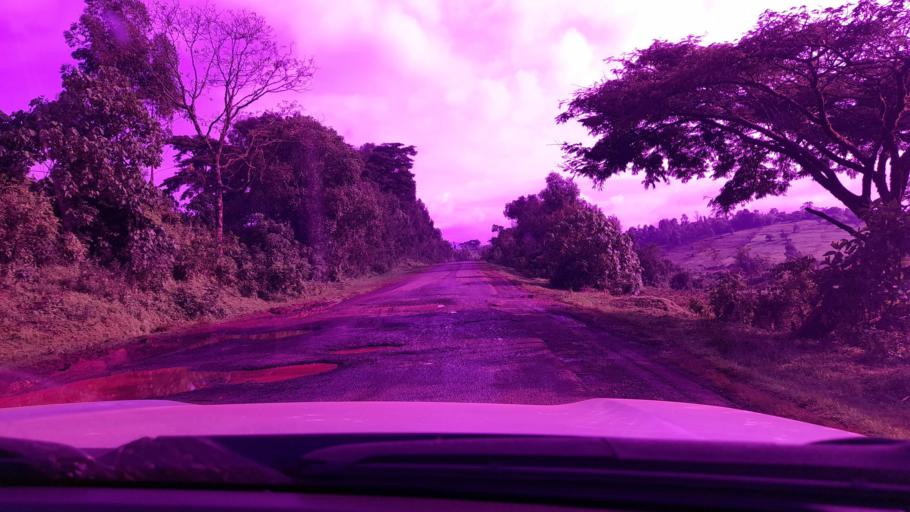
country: ET
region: Oromiya
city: Bedele
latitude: 8.1934
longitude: 36.4436
